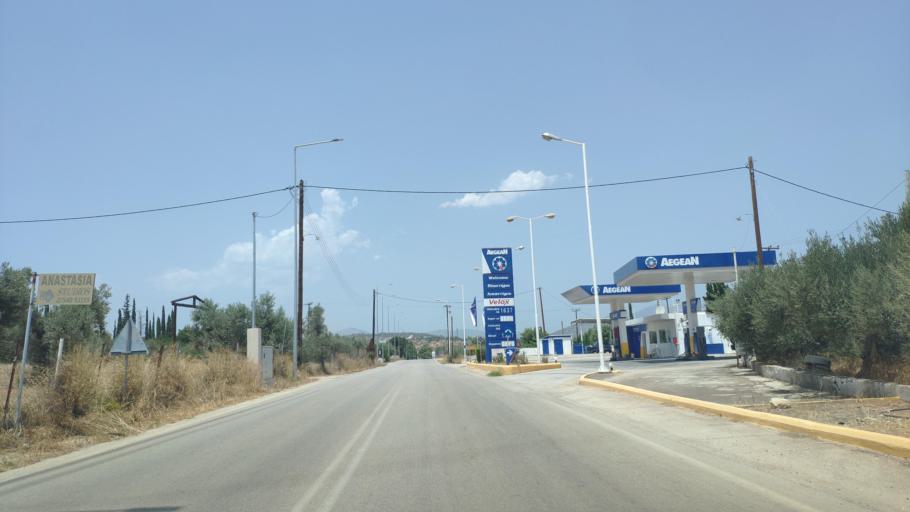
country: GR
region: Peloponnese
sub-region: Nomos Argolidos
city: Porto Cheli
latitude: 37.3433
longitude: 23.1576
